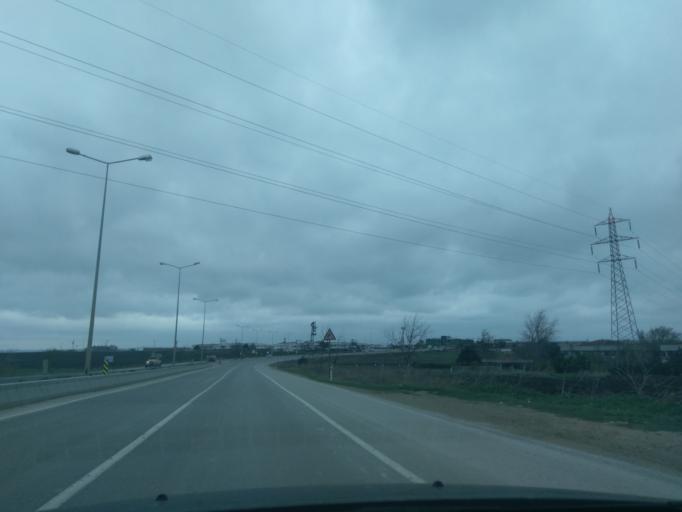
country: TR
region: Istanbul
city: Muratbey
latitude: 41.1231
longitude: 28.4895
